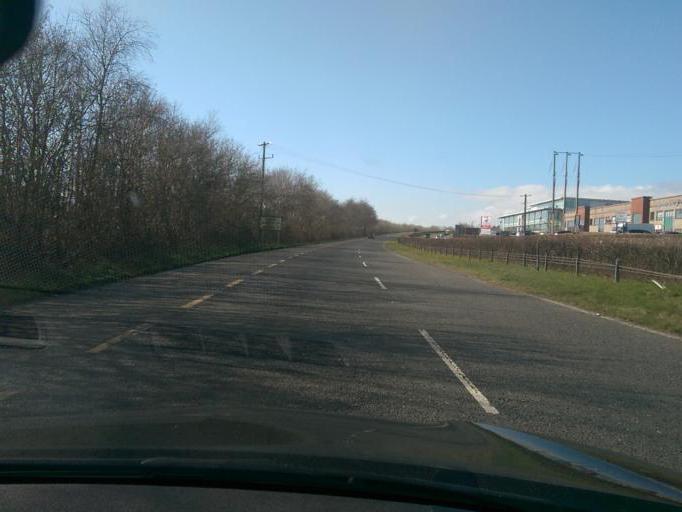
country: IE
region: Connaught
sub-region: County Galway
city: Oranmore
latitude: 53.2769
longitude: -8.9284
